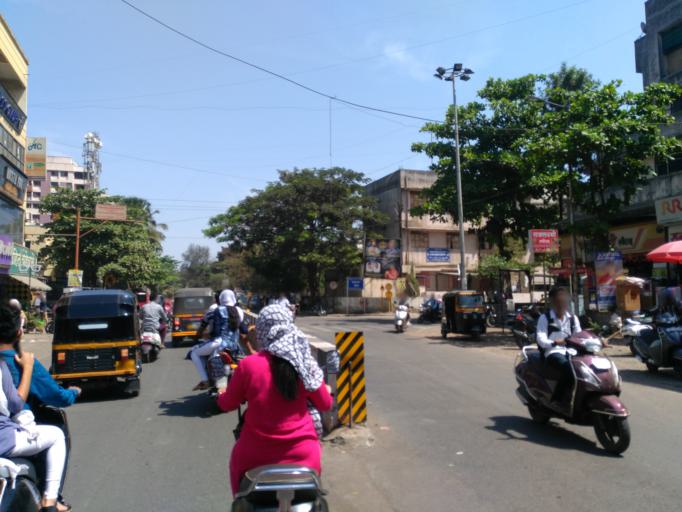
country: IN
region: Maharashtra
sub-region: Pune Division
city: Pune
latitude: 18.4537
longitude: 73.8511
